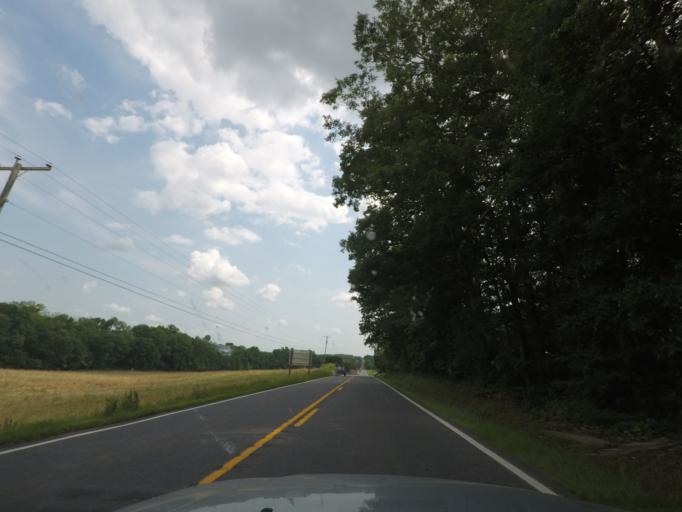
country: US
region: Virginia
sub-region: Orange County
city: Gordonsville
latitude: 38.0672
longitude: -78.1875
